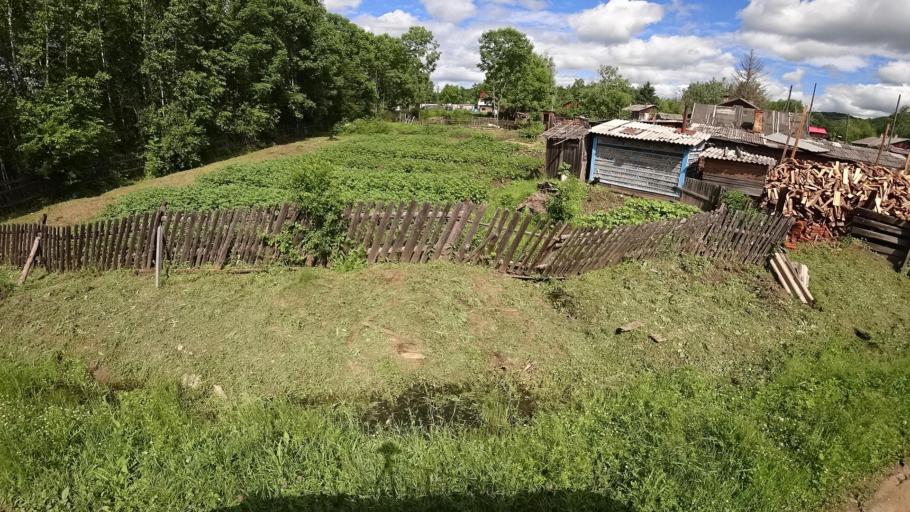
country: RU
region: Khabarovsk Krai
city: Litovko
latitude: 49.3665
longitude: 135.1691
